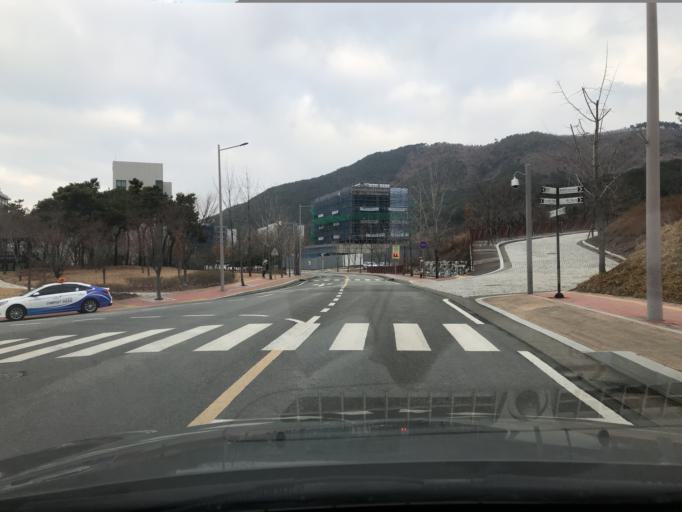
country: KR
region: Daegu
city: Hwawon
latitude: 35.7053
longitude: 128.4600
